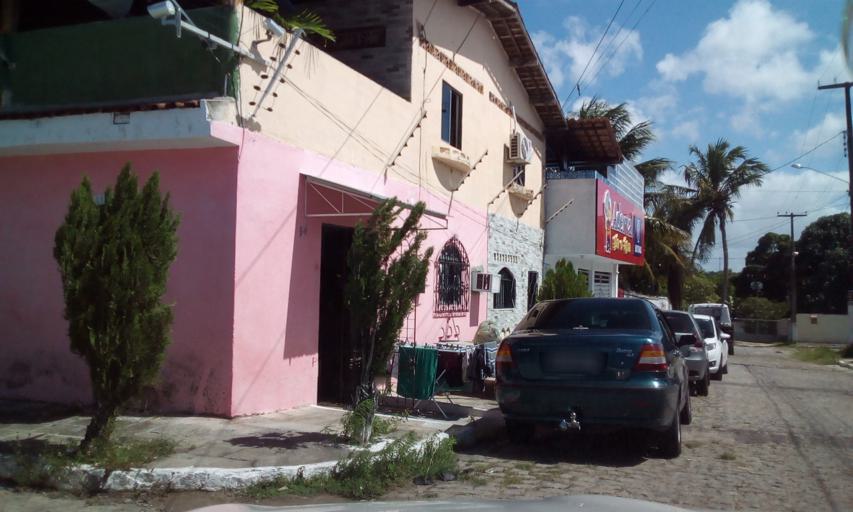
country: BR
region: Paraiba
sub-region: Joao Pessoa
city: Joao Pessoa
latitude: -7.1863
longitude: -34.8482
